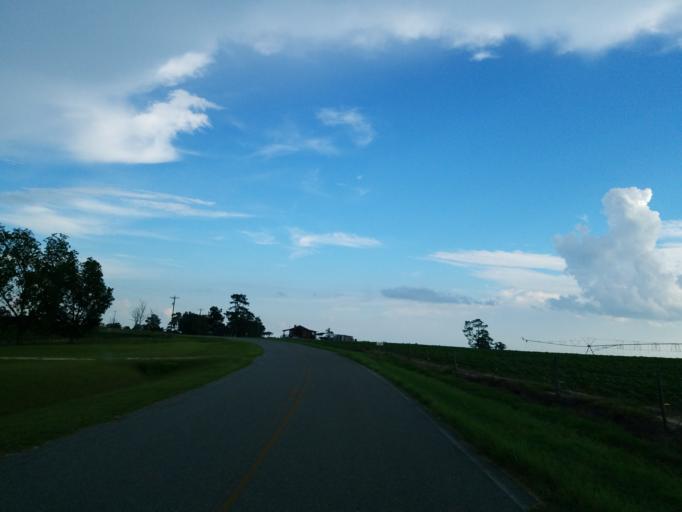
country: US
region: Georgia
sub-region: Tift County
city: Omega
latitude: 31.2685
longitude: -83.5187
